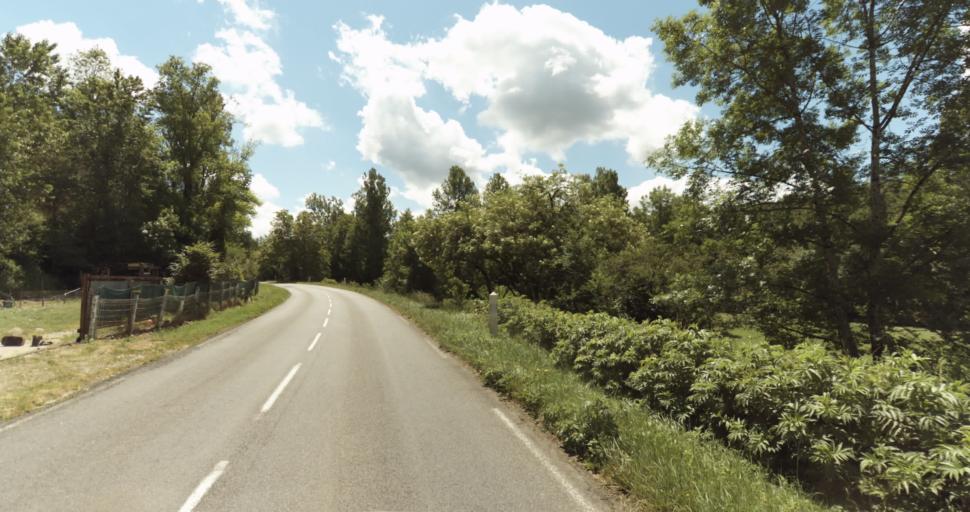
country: FR
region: Aquitaine
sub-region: Departement de la Dordogne
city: Beaumont-du-Perigord
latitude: 44.7883
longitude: 0.7599
